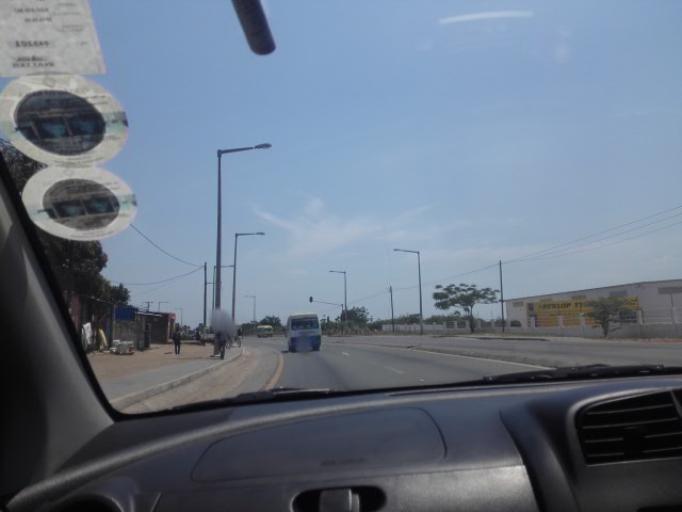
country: MZ
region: Maputo City
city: Maputo
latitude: -25.9189
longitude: 32.5646
